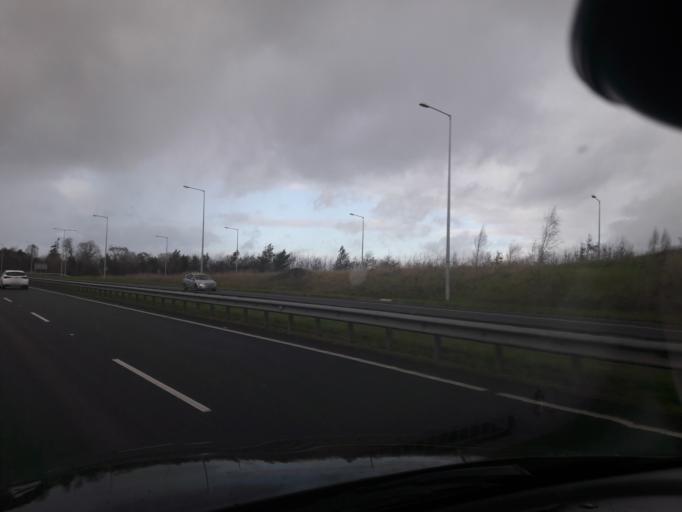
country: IE
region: Leinster
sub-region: An Mhi
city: Ashbourne
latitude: 53.4891
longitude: -6.3898
